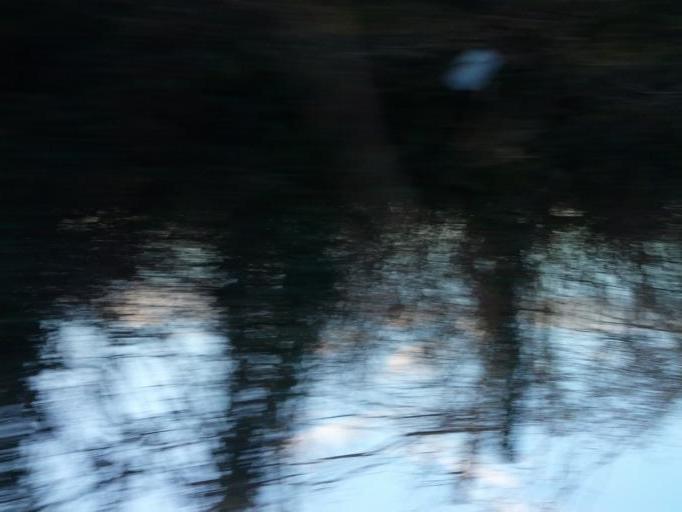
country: IE
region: Connaught
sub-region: County Galway
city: Loughrea
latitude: 53.3234
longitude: -8.6106
